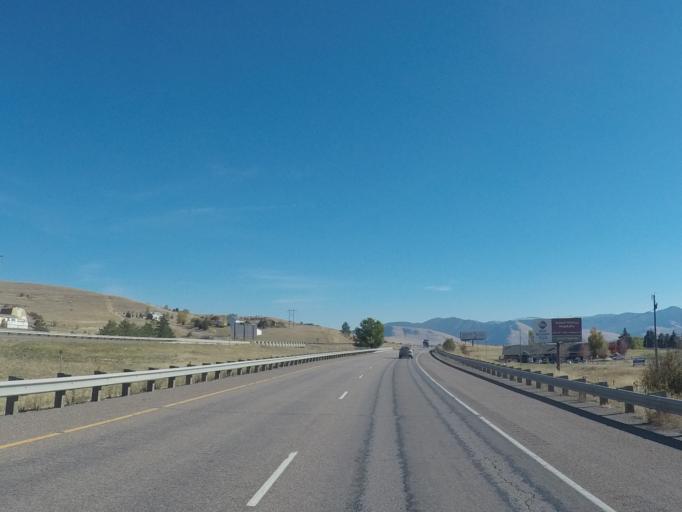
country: US
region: Montana
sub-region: Missoula County
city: Orchard Homes
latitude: 46.9367
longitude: -114.0956
